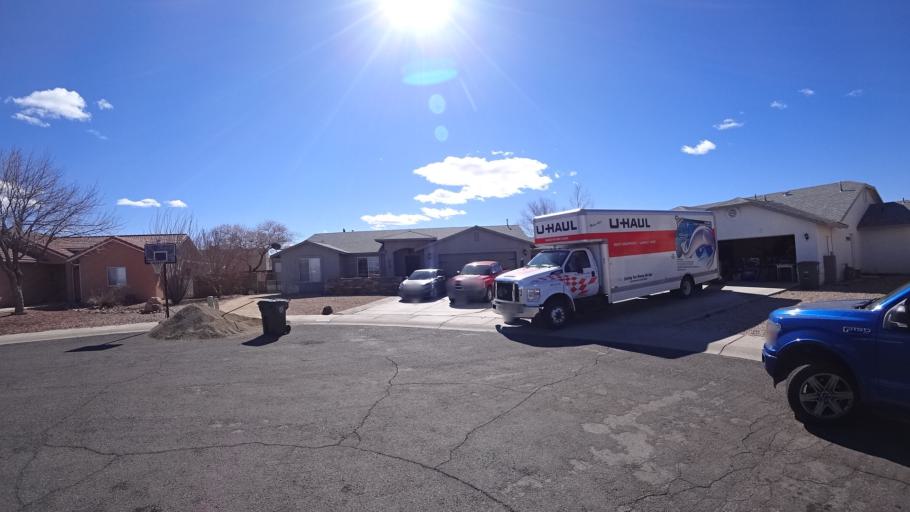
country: US
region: Arizona
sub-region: Mohave County
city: Kingman
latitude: 35.1918
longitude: -114.0094
